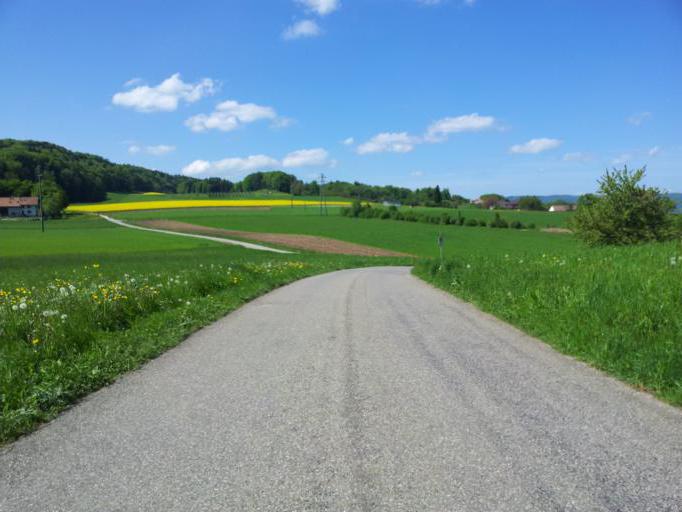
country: CH
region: Aargau
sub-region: Bezirk Bremgarten
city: Rudolfstetten
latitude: 47.3903
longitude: 8.3748
